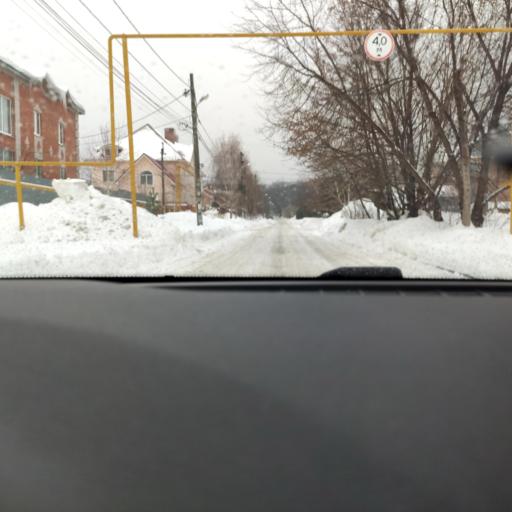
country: RU
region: Samara
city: Petra-Dubrava
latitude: 53.3148
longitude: 50.2788
